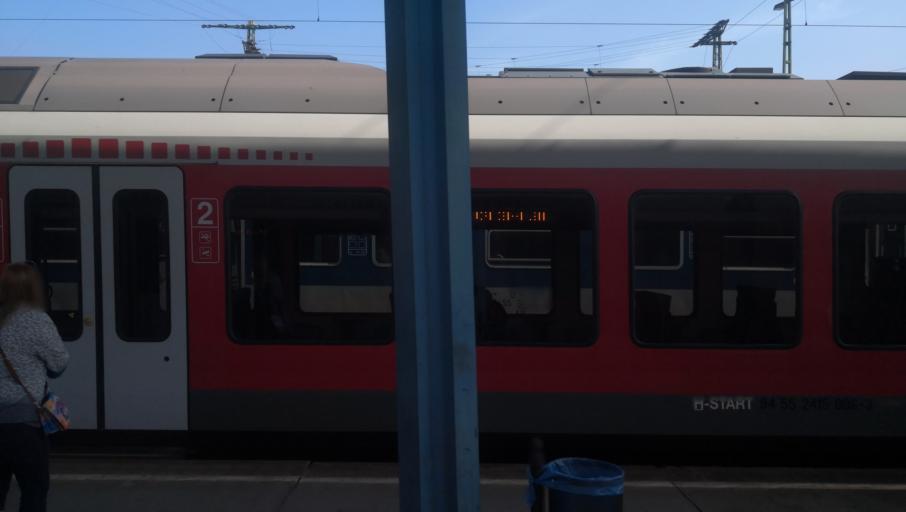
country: HU
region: Budapest
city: Budapest VII. keruelet
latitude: 47.5007
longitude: 19.0883
